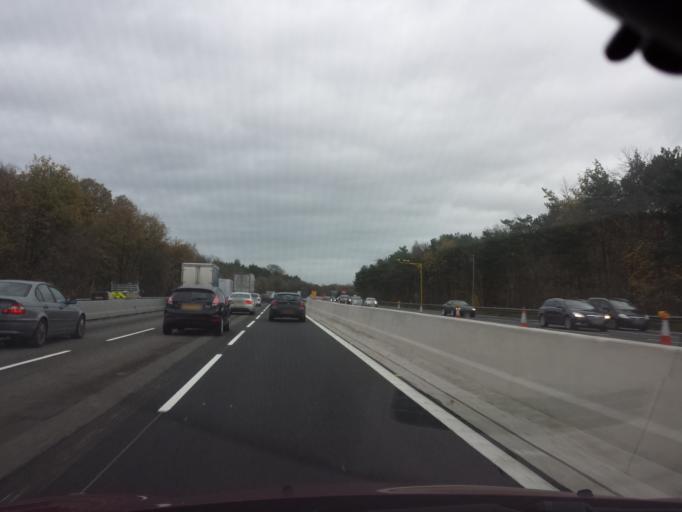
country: GB
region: England
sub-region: Surrey
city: Windlesham
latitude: 51.3647
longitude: -0.6394
